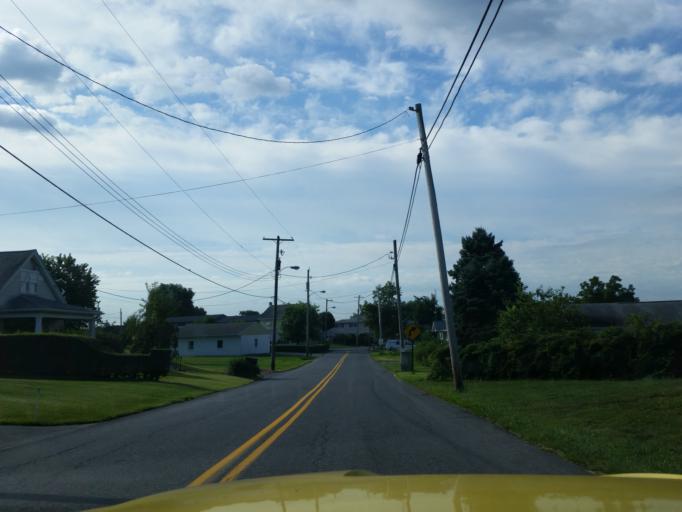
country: US
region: Pennsylvania
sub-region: Lebanon County
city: Fredericksburg
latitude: 40.4492
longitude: -76.4326
